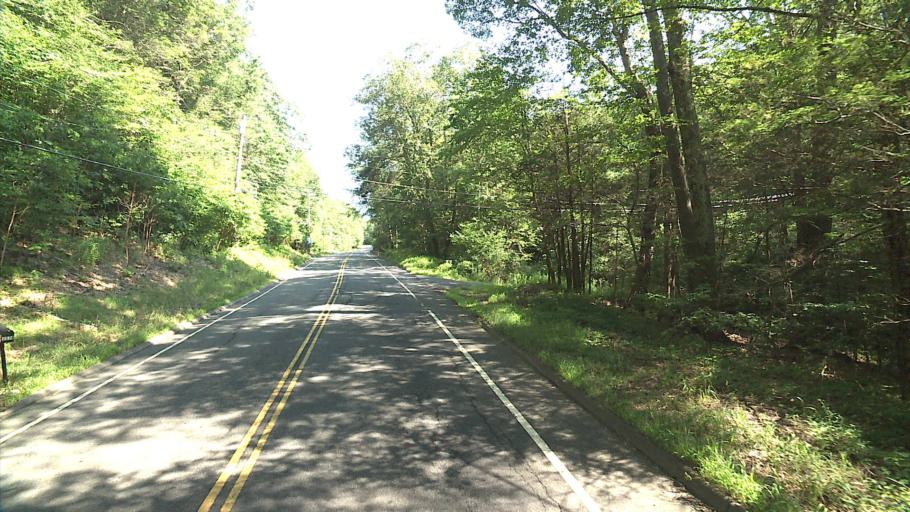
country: US
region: Connecticut
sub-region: Hartford County
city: North Granby
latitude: 41.9774
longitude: -72.8890
